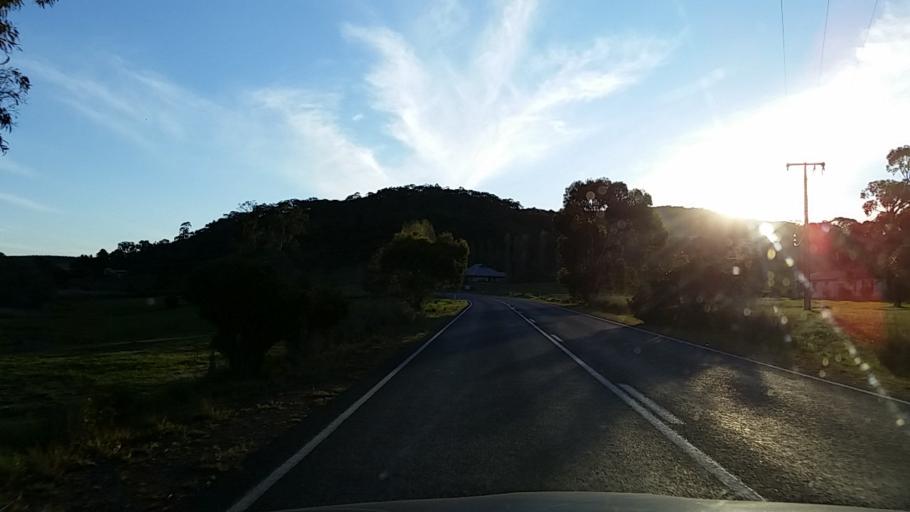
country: AU
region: South Australia
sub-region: Alexandrina
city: Mount Compass
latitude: -35.3401
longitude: 138.6538
